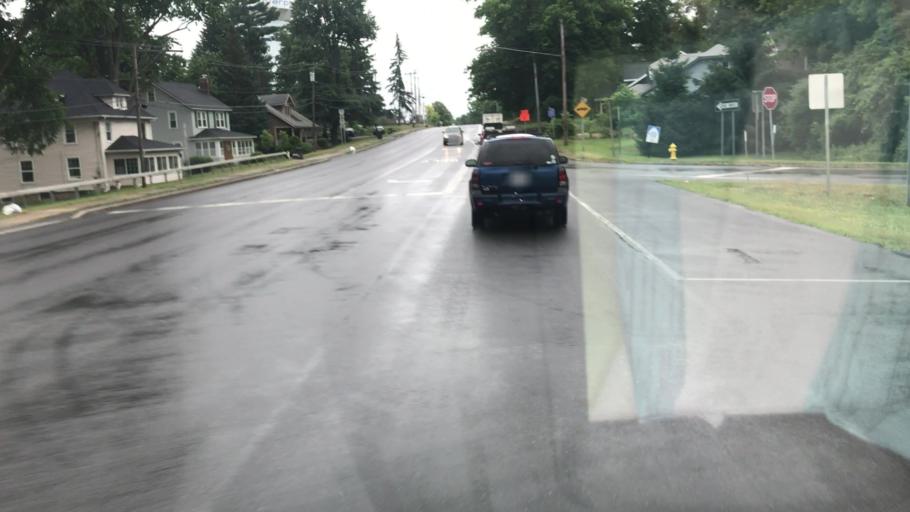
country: US
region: New York
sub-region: Onondaga County
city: Liverpool
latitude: 43.1140
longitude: -76.2127
